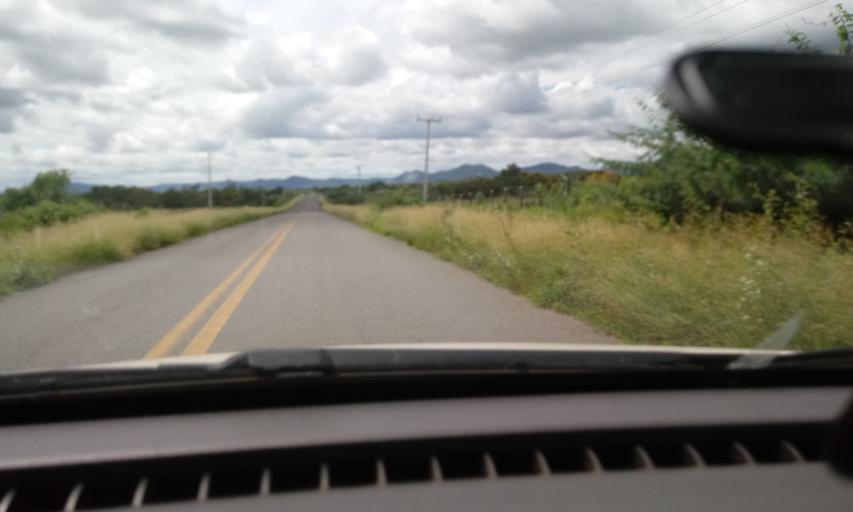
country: BR
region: Bahia
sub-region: Guanambi
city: Guanambi
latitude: -13.9582
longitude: -42.8547
